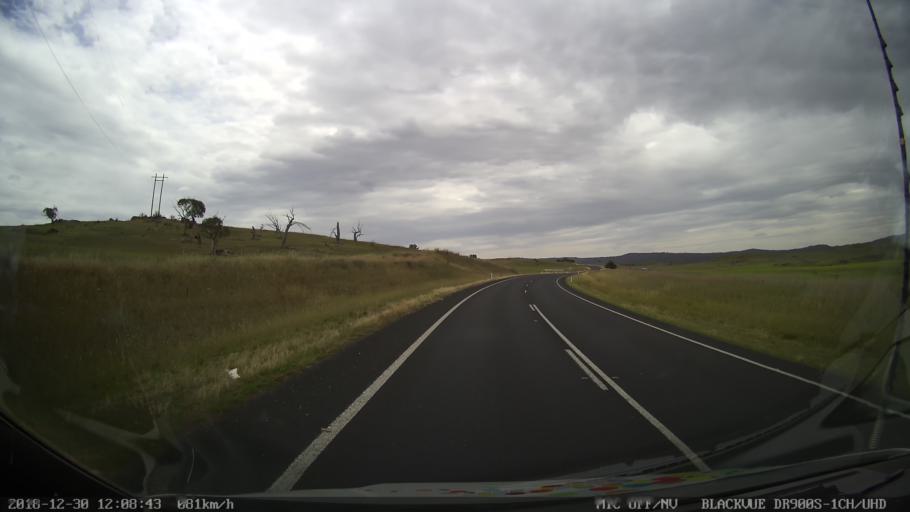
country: AU
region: New South Wales
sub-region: Snowy River
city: Jindabyne
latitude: -36.3920
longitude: 148.5946
